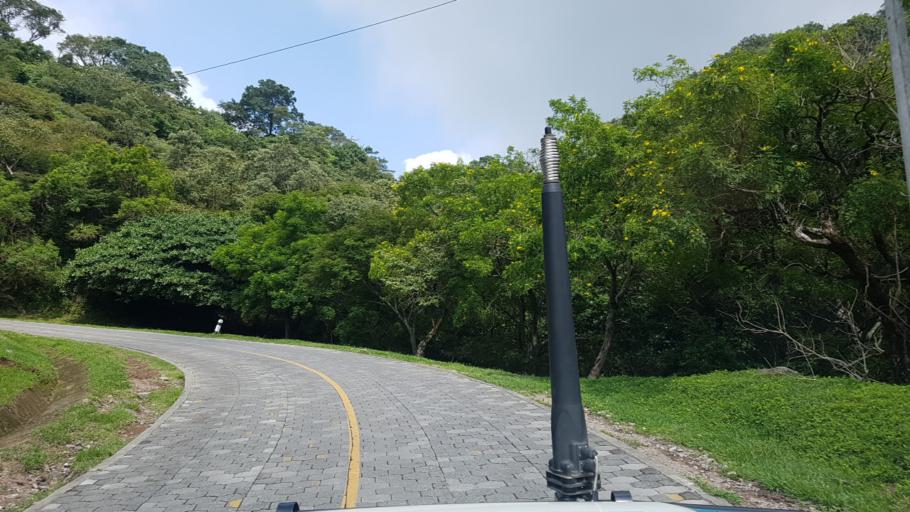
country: NI
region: Leon
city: Santa Rosa del Penon
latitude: 12.9368
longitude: -86.3387
